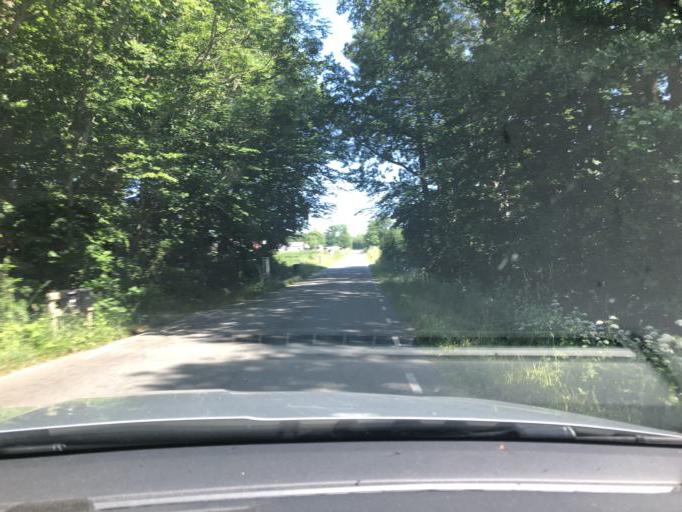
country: SE
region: Blekinge
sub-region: Karlshamns Kommun
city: Morrum
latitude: 56.1730
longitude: 14.6410
